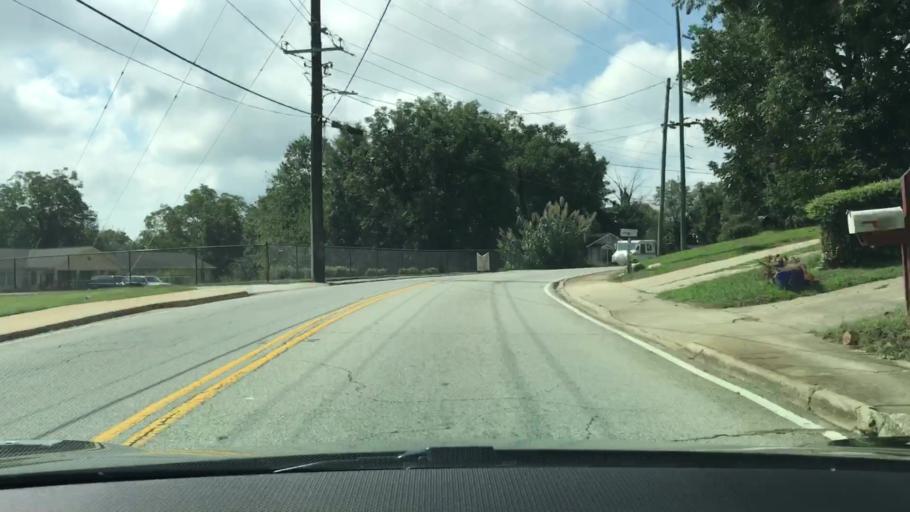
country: US
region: Georgia
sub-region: Hall County
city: Gainesville
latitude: 34.2987
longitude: -83.8121
